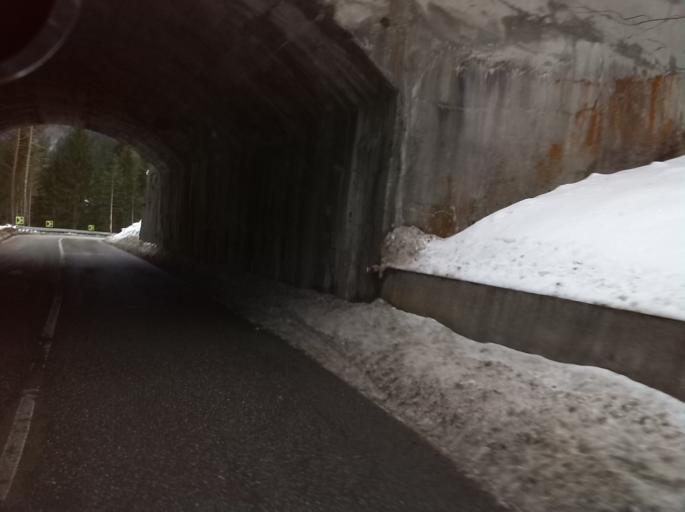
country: IT
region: Friuli Venezia Giulia
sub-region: Provincia di Udine
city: Tarvisio
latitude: 46.5048
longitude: 13.6202
